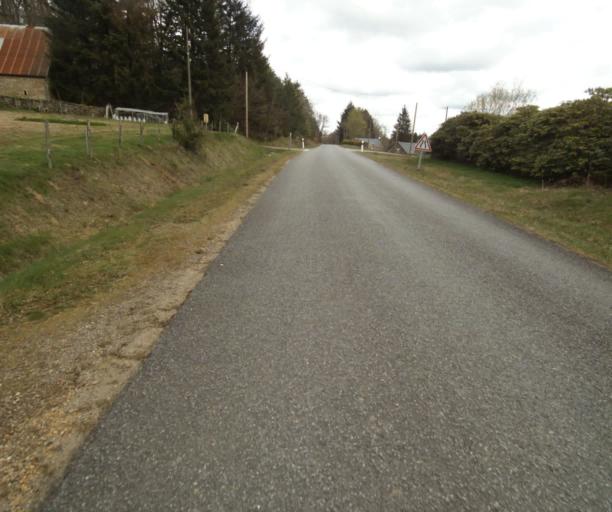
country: FR
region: Limousin
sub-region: Departement de la Correze
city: Correze
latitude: 45.3598
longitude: 1.9268
